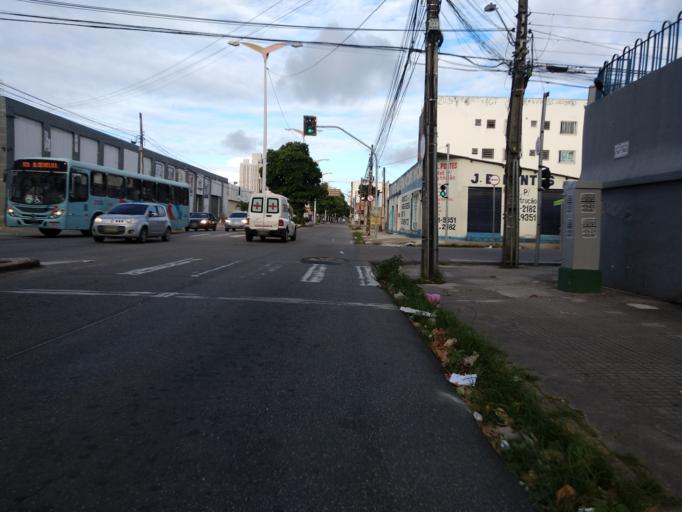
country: BR
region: Ceara
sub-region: Fortaleza
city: Fortaleza
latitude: -3.7287
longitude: -38.5392
